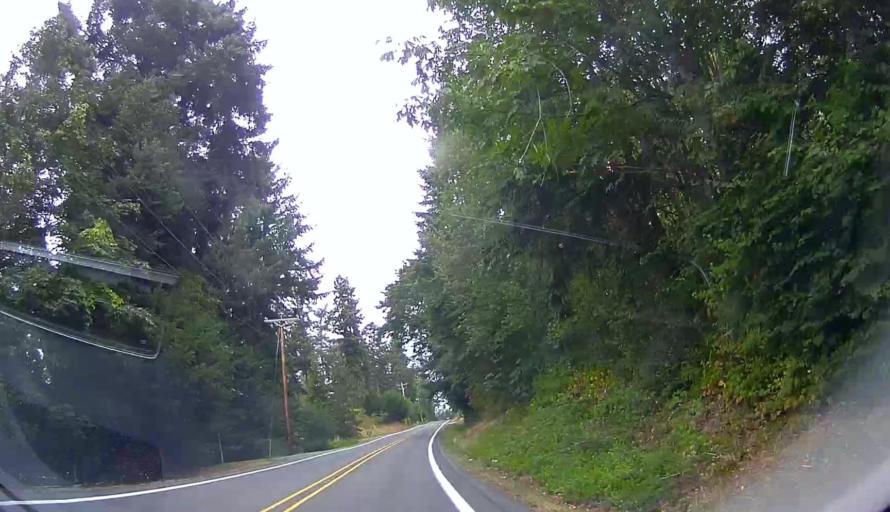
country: US
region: Washington
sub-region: Snohomish County
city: Warm Beach
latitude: 48.1467
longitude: -122.3603
